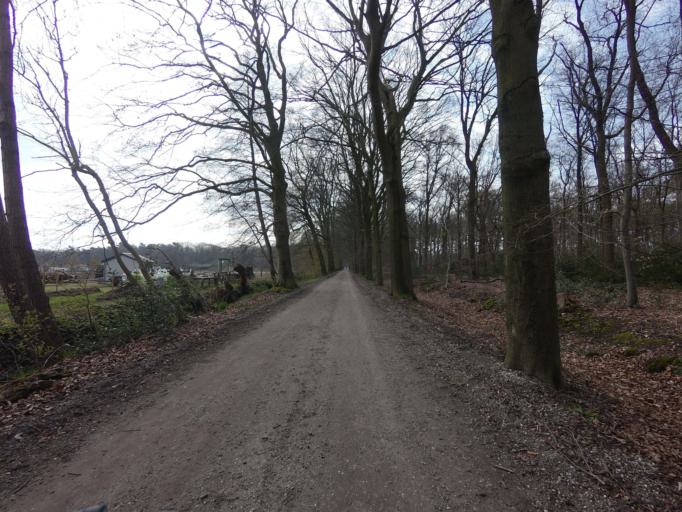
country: NL
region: Gelderland
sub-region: Gemeente Harderwijk
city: Harderwijk
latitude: 52.3483
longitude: 5.7029
